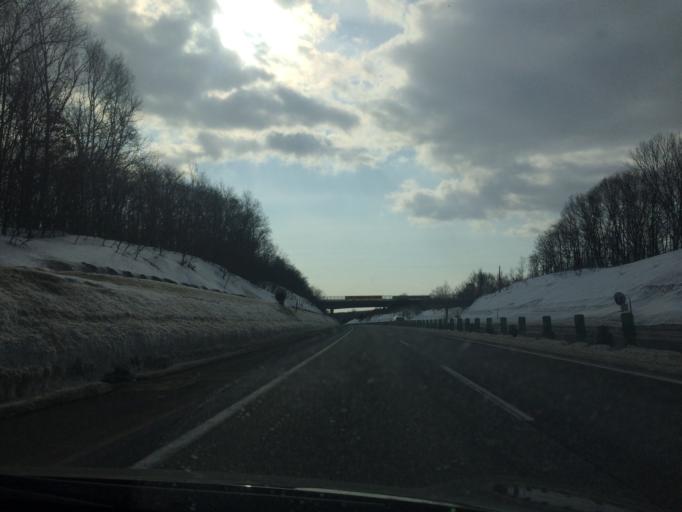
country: JP
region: Hokkaido
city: Kitahiroshima
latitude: 42.9385
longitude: 141.5233
